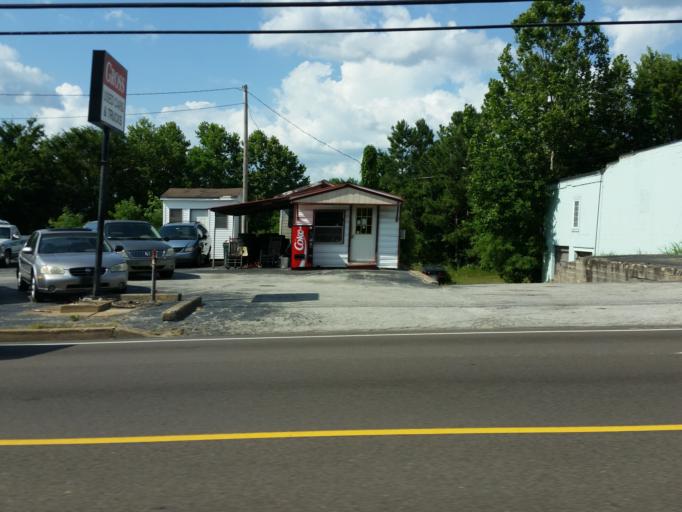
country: US
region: Tennessee
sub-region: Henderson County
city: Lexington
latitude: 35.6547
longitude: -88.4011
